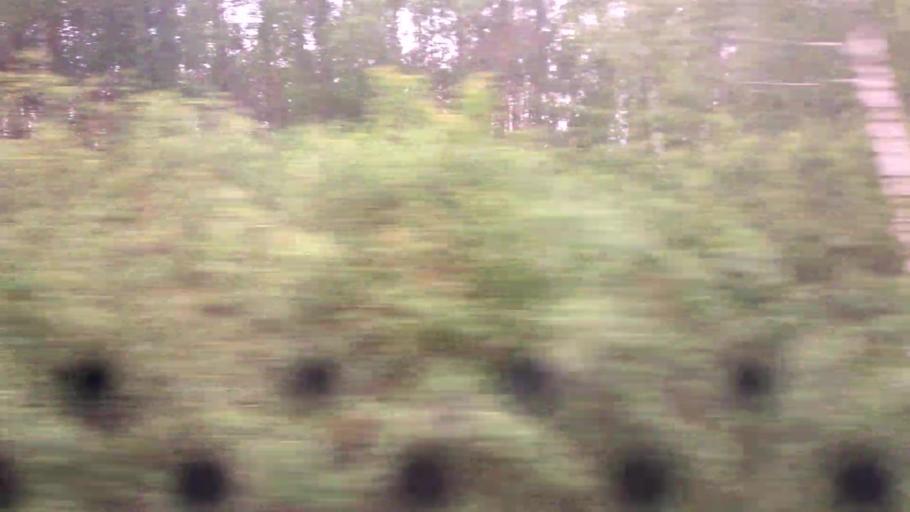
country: RU
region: Moskovskaya
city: Kolomna
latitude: 55.0542
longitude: 38.8675
